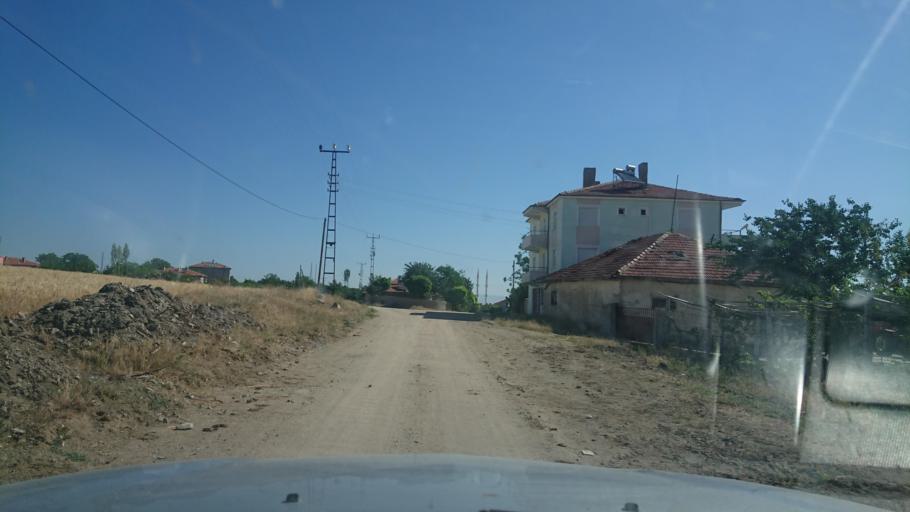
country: TR
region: Aksaray
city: Agacoren
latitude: 38.8647
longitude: 33.9131
